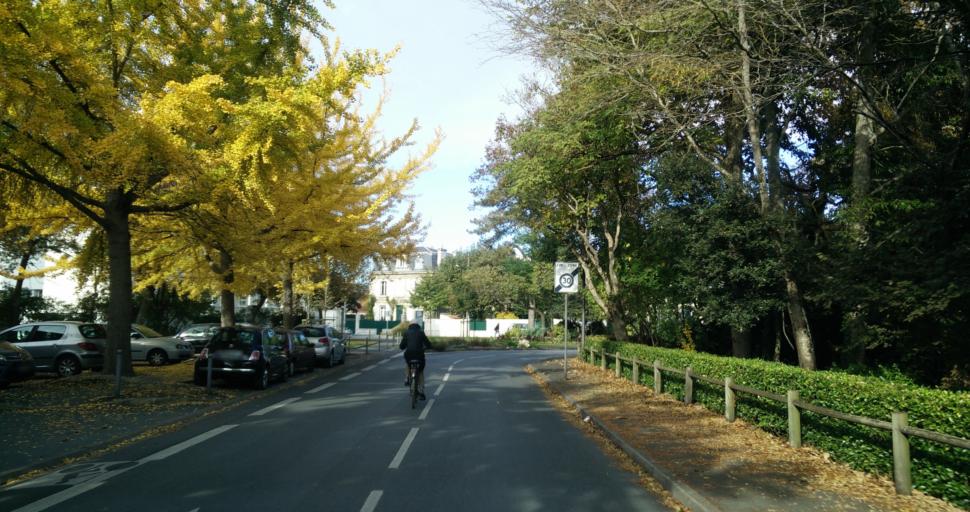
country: FR
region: Poitou-Charentes
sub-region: Departement de la Charente-Maritime
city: La Rochelle
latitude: 46.1617
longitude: -1.1585
